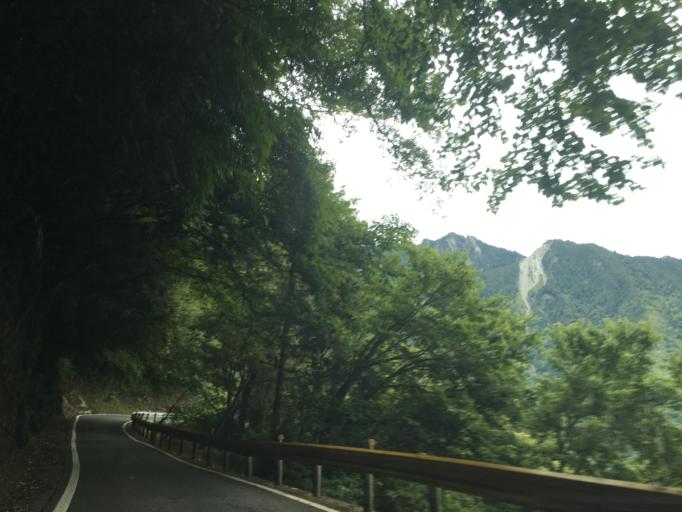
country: TW
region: Taiwan
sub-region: Hualien
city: Hualian
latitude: 24.1822
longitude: 121.3935
